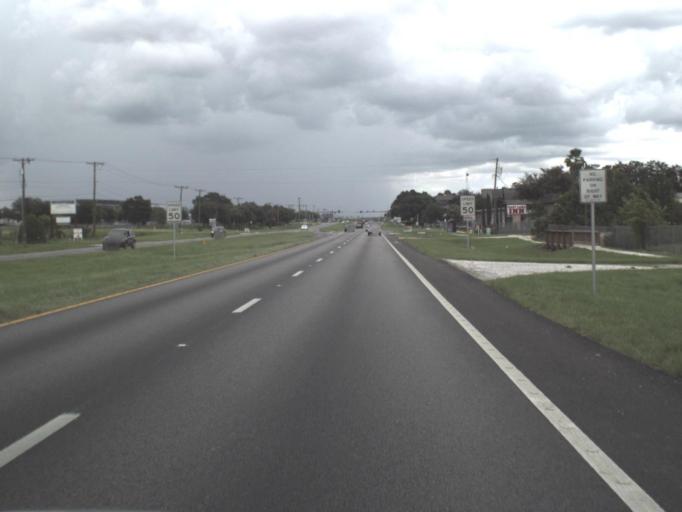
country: US
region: Florida
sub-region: Hillsborough County
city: East Lake-Orient Park
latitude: 27.9961
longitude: -82.3828
